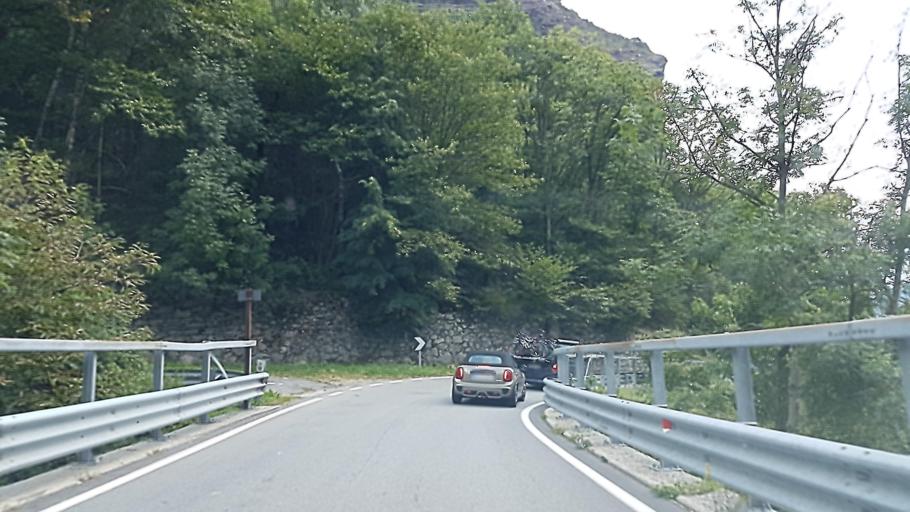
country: IT
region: Lombardy
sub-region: Provincia di Sondrio
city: San Giacomo Filippo
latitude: 46.3545
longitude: 9.3658
